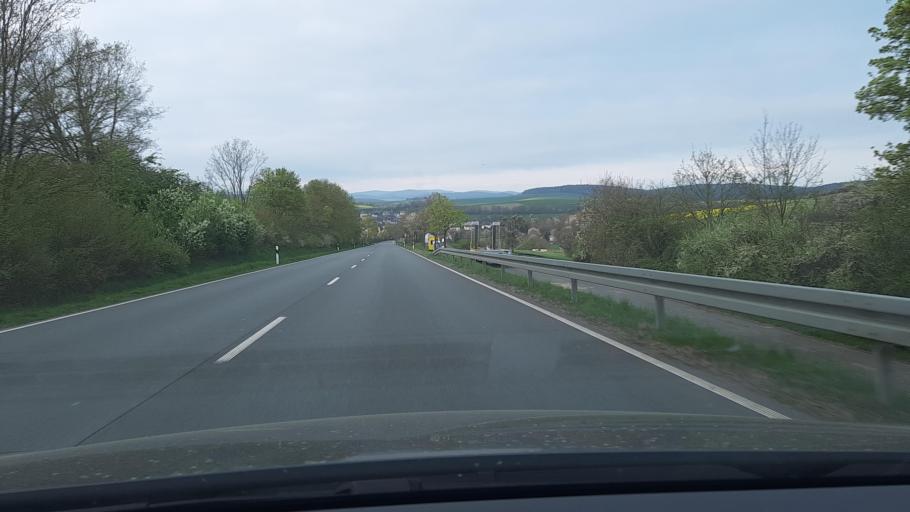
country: DE
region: Hesse
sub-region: Regierungsbezirk Darmstadt
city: Gravenwiesbach
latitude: 50.3969
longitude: 8.4607
